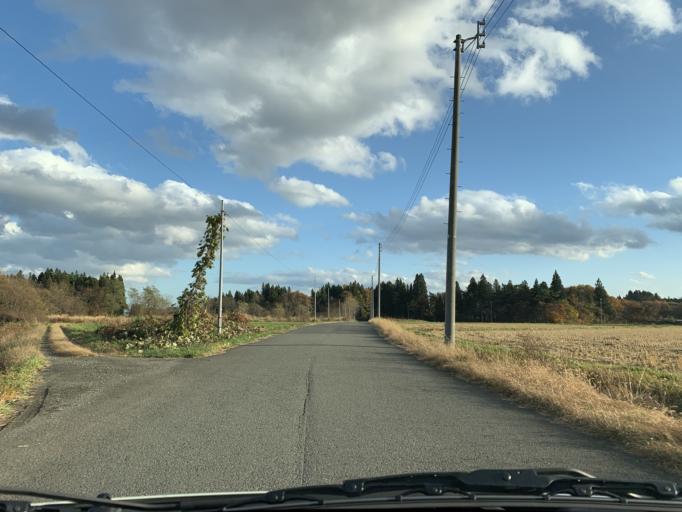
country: JP
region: Iwate
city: Mizusawa
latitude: 39.1185
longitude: 140.9973
